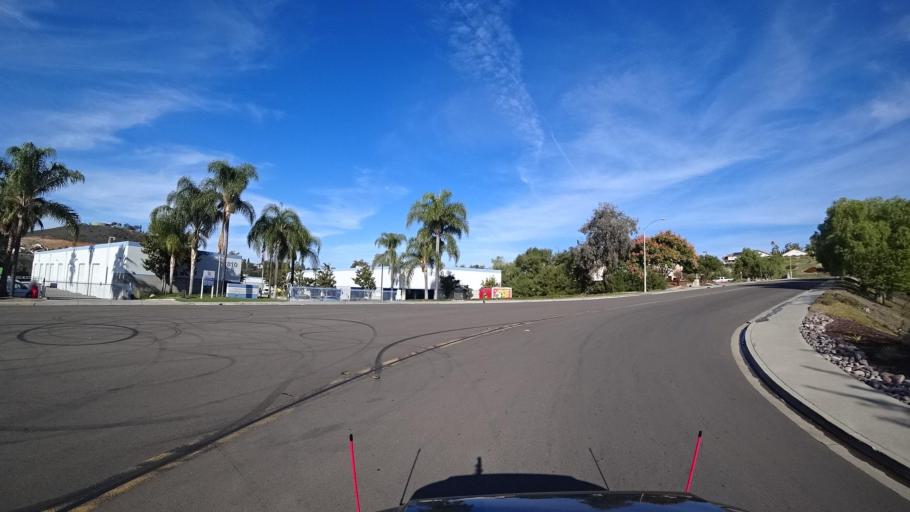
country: US
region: California
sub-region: San Diego County
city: Spring Valley
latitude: 32.7292
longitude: -116.9689
